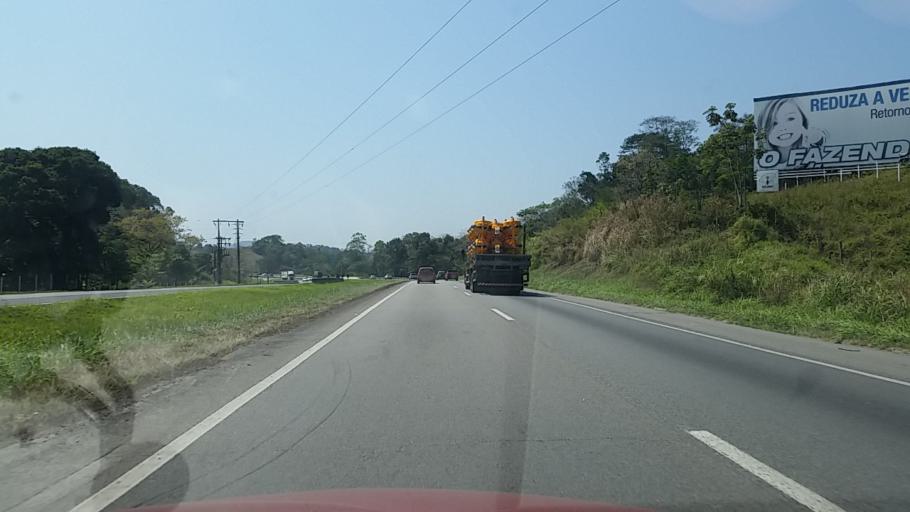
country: BR
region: Sao Paulo
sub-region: Miracatu
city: Miracatu
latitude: -24.2638
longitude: -47.3822
